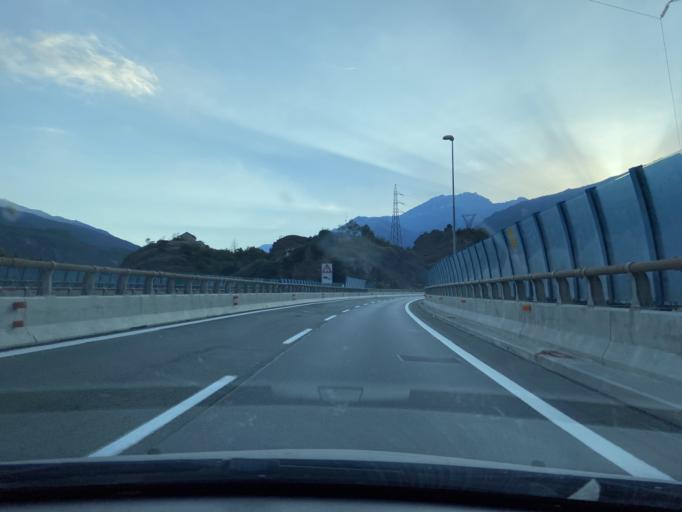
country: IT
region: Piedmont
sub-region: Provincia di Torino
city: Susa
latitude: 45.1424
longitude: 7.0569
